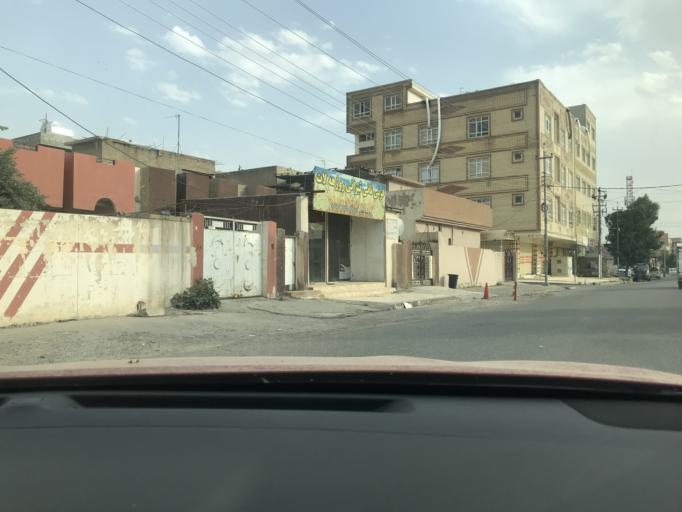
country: IQ
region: Arbil
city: Erbil
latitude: 36.1793
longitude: 43.9779
